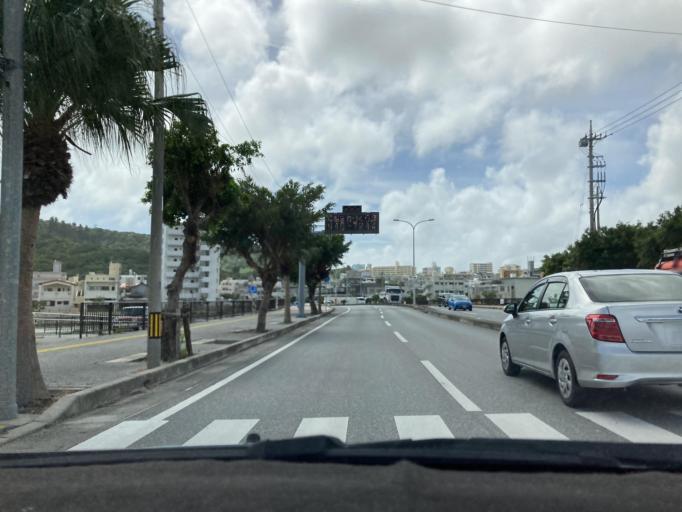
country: JP
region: Okinawa
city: Ginowan
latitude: 26.2036
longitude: 127.7610
